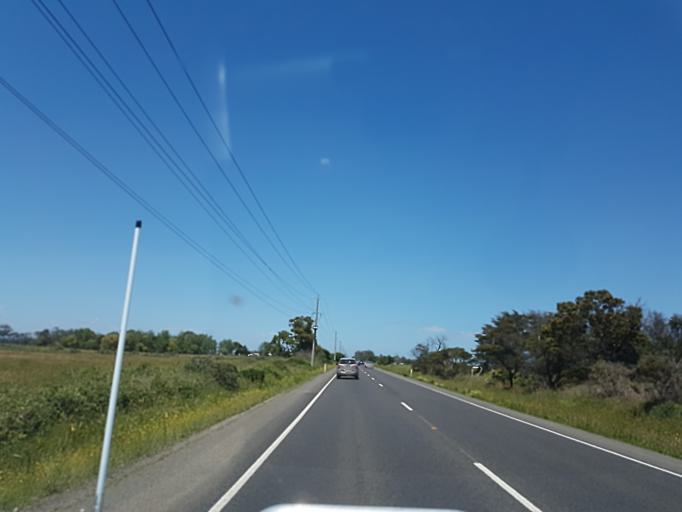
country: AU
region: Victoria
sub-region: Cardinia
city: Pakenham South
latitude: -38.1473
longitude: 145.4869
